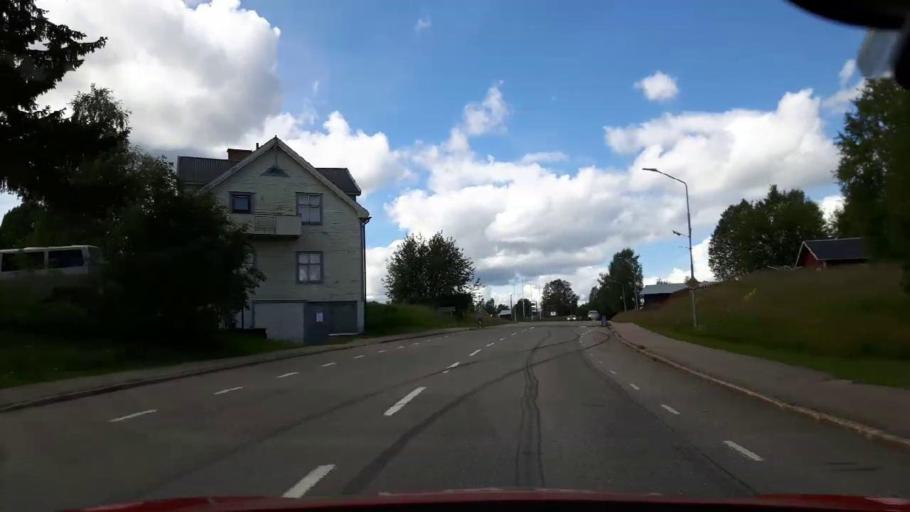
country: SE
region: Jaemtland
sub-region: Harjedalens Kommun
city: Sveg
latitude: 61.8505
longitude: 14.0738
